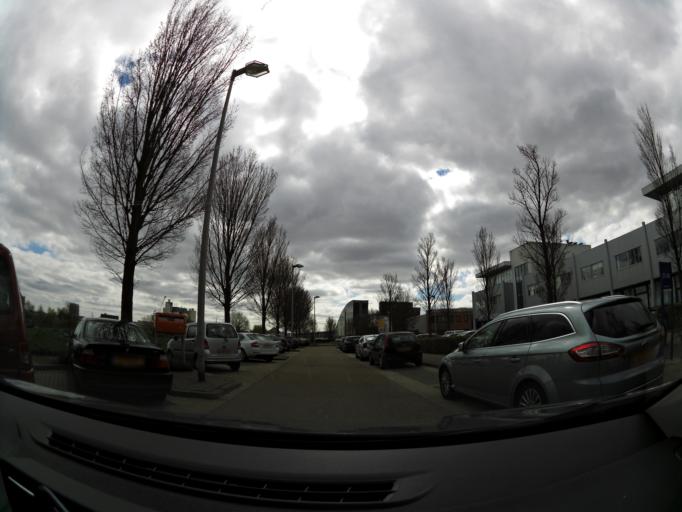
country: NL
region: South Holland
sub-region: Gemeente Rotterdam
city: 's-Gravenland
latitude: 51.9104
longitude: 4.5482
